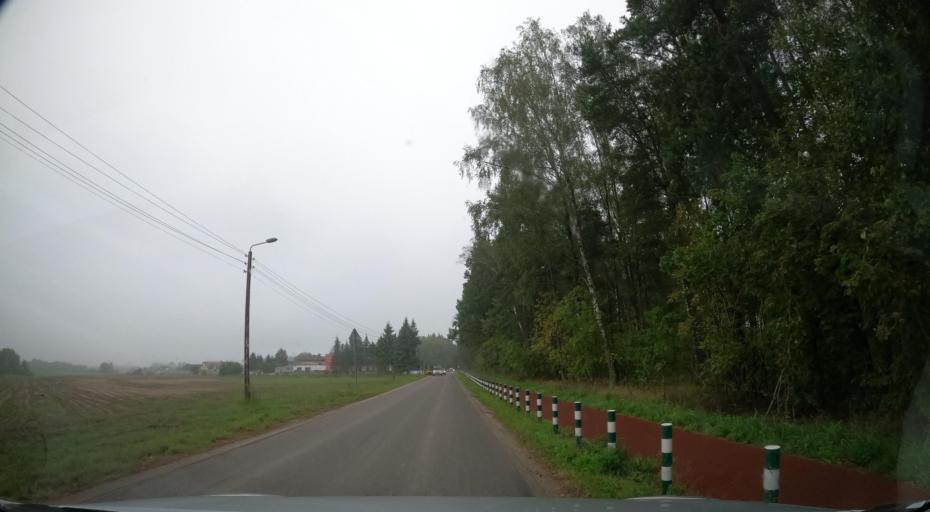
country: PL
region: Pomeranian Voivodeship
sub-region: Powiat kartuski
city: Chwaszczyno
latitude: 54.4368
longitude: 18.4182
